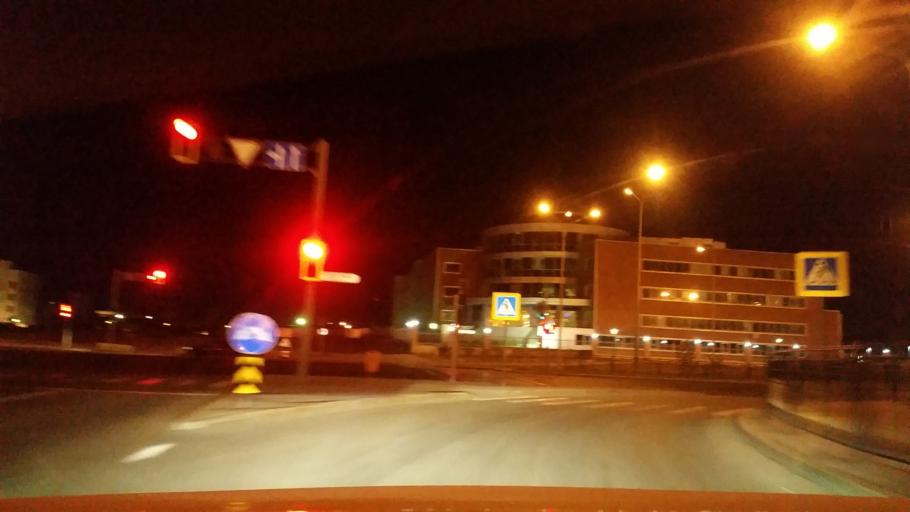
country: KZ
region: Astana Qalasy
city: Astana
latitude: 51.1262
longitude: 71.4764
